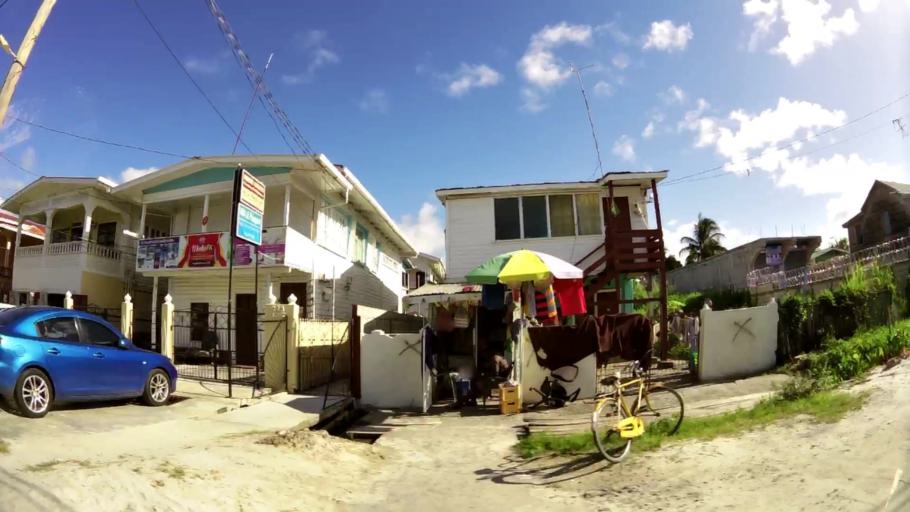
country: GY
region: Demerara-Mahaica
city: Georgetown
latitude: 6.8133
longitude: -58.1416
